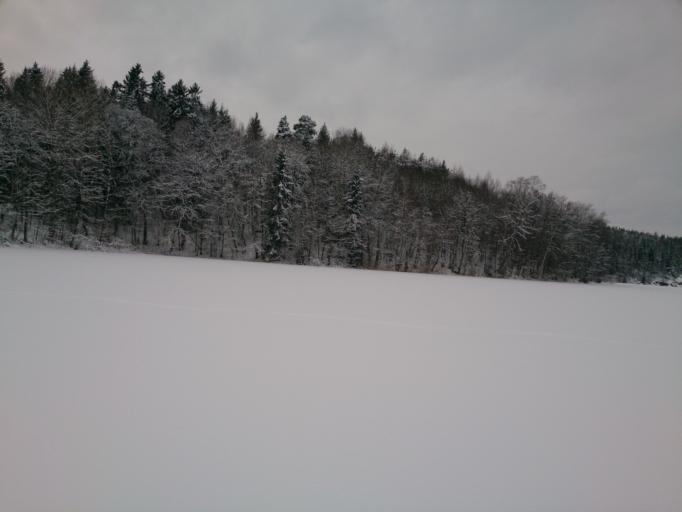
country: SE
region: OEstergoetland
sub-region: Atvidabergs Kommun
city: Atvidaberg
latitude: 58.3396
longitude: 16.0218
